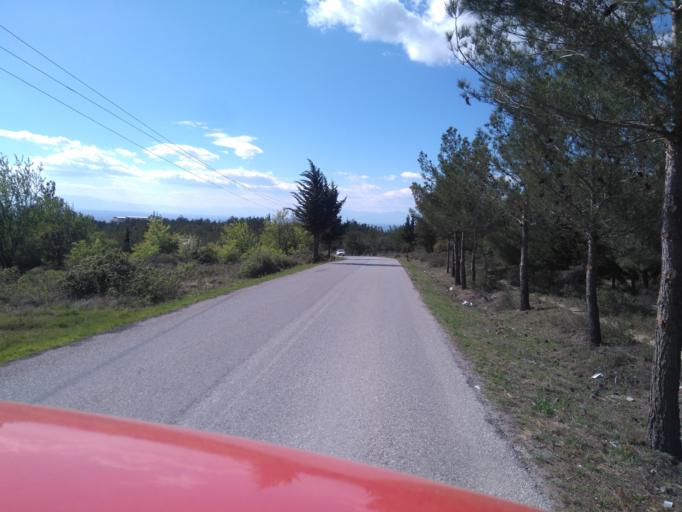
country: GR
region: Central Macedonia
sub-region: Nomos Thessalonikis
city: Pefka
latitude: 40.6459
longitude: 22.9930
